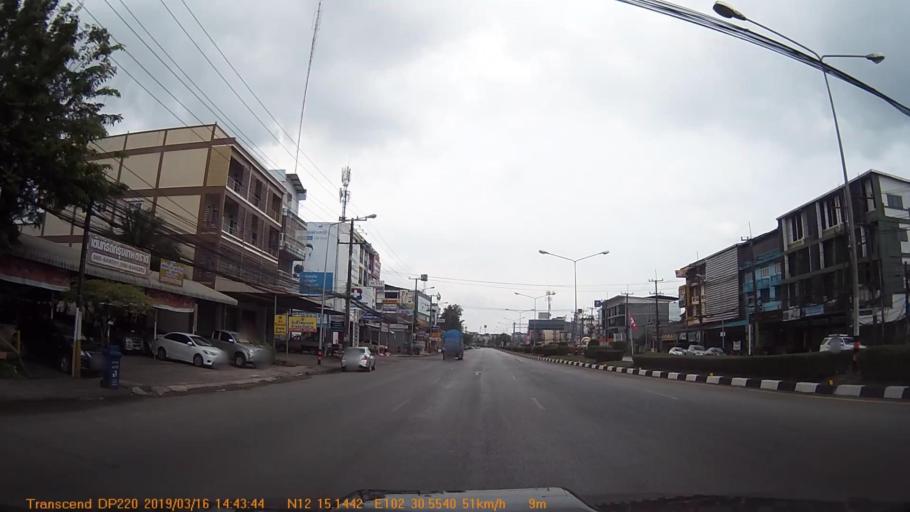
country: TH
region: Trat
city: Trat
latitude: 12.2526
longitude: 102.5092
